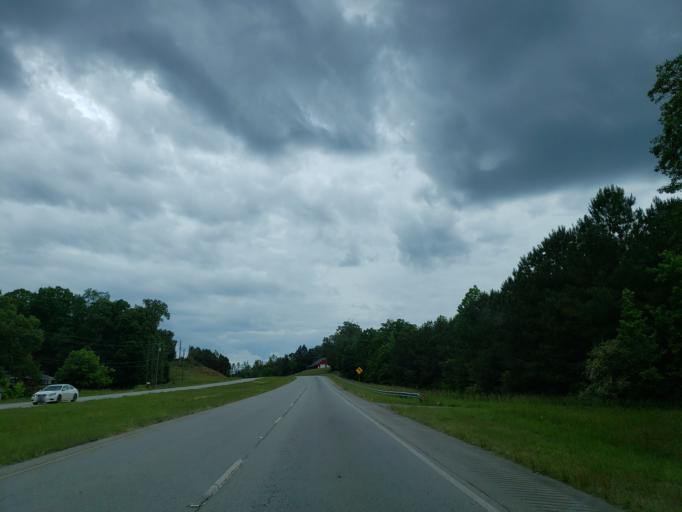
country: US
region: Georgia
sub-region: Polk County
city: Cedartown
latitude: 33.9395
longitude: -85.2455
